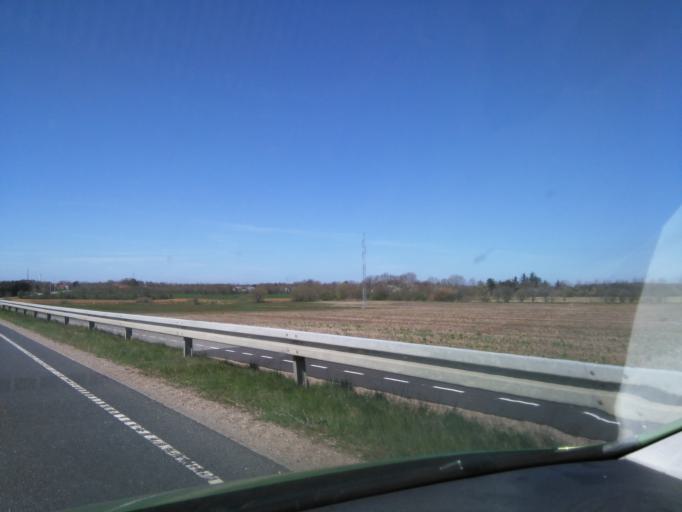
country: DK
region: South Denmark
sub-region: Varde Kommune
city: Oksbol
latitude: 55.6183
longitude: 8.3131
